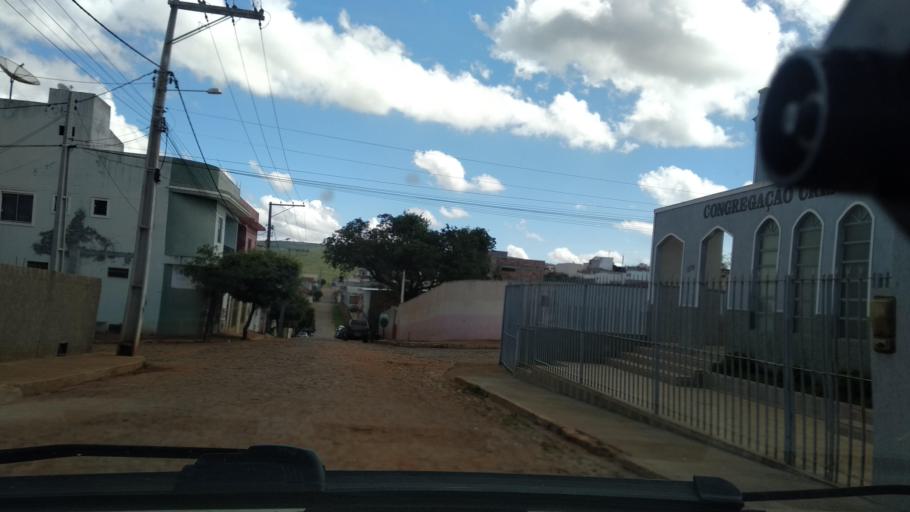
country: BR
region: Bahia
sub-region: Caetite
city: Caetite
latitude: -14.0601
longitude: -42.4854
